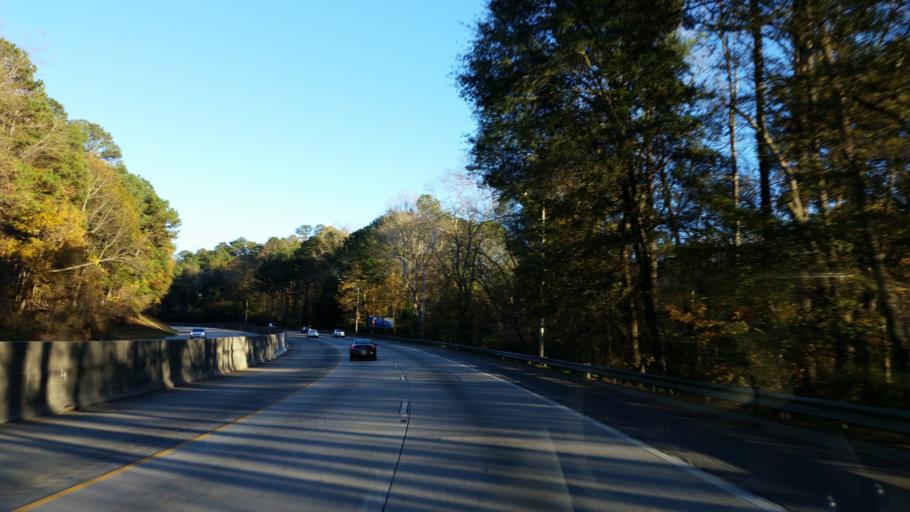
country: US
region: Georgia
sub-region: Fulton County
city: East Point
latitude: 33.6974
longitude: -84.4648
